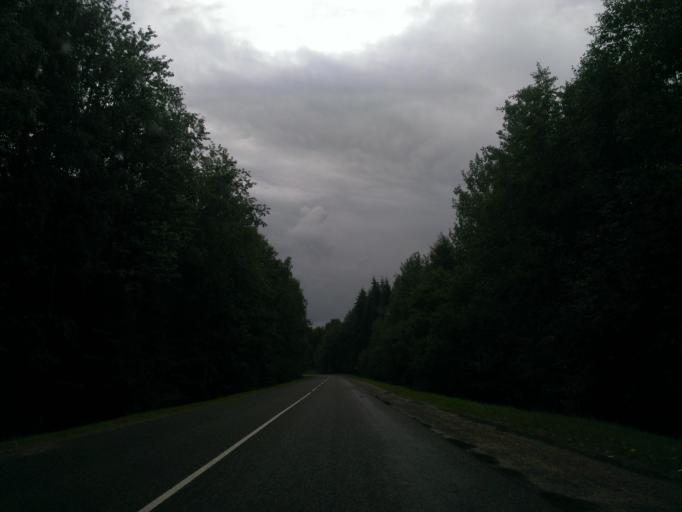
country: LV
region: Kegums
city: Kegums
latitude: 56.7559
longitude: 24.7388
